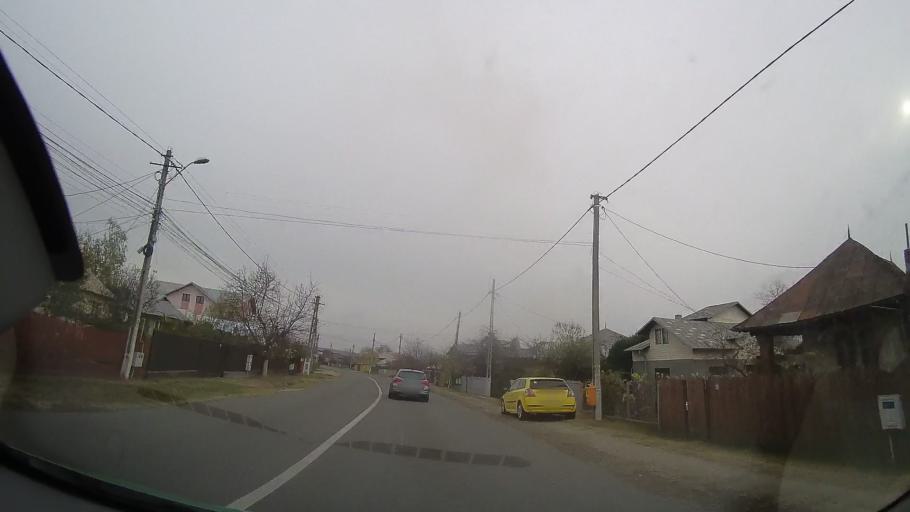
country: RO
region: Prahova
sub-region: Oras Baicoi
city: Tintea
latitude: 45.0311
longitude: 25.9064
